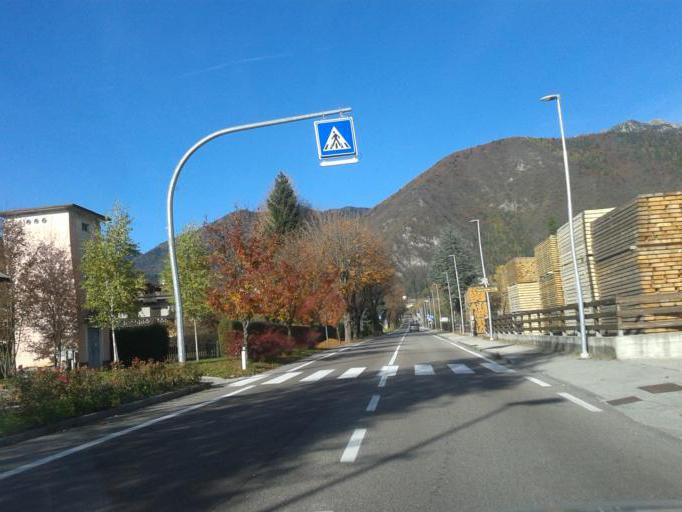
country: IT
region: Trentino-Alto Adige
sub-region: Provincia di Trento
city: Pieve di Ledro
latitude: 45.8898
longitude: 10.7286
